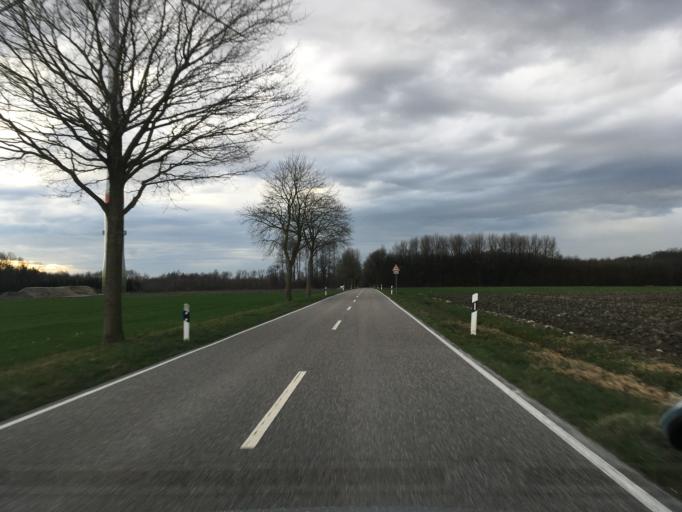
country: DE
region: North Rhine-Westphalia
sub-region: Regierungsbezirk Munster
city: Schoppingen
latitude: 52.0624
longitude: 7.1757
